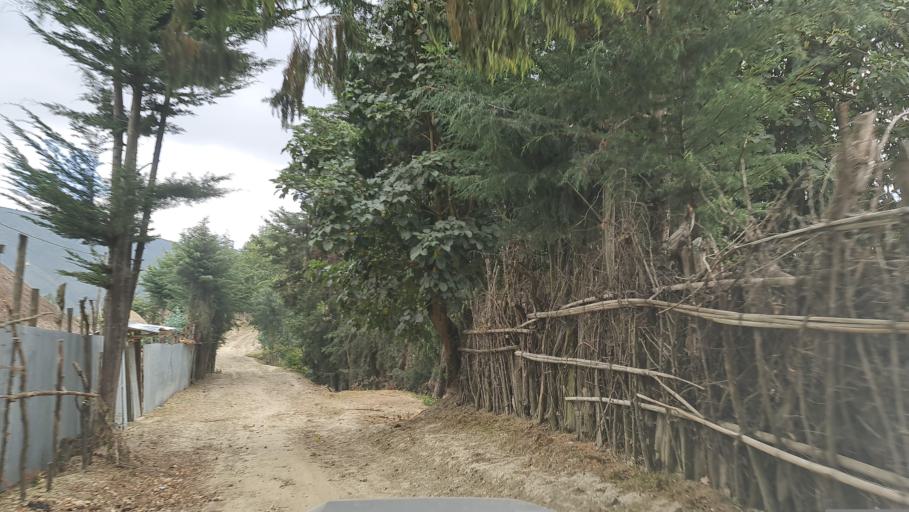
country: ET
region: Oromiya
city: Hagere Hiywet
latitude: 8.7985
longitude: 37.8880
